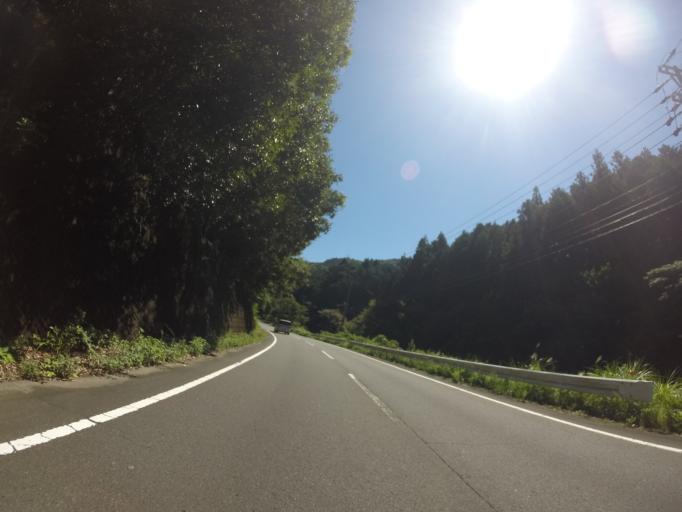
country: JP
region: Shizuoka
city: Kanaya
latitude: 34.9046
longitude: 138.1181
